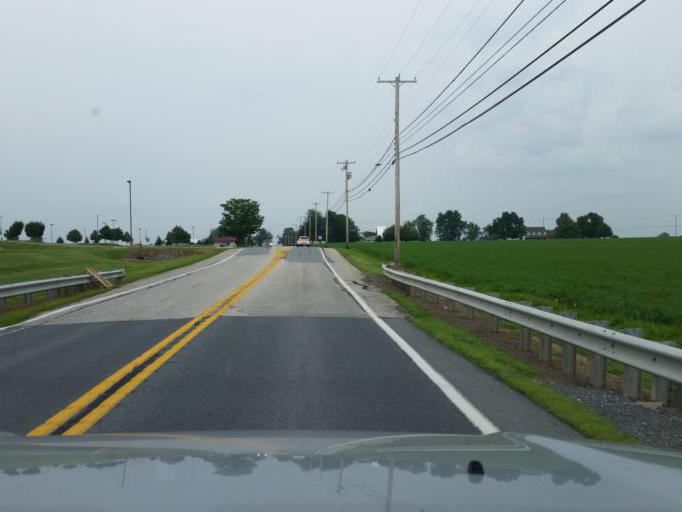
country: US
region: Pennsylvania
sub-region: Lancaster County
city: Salunga
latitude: 40.1277
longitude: -76.4563
